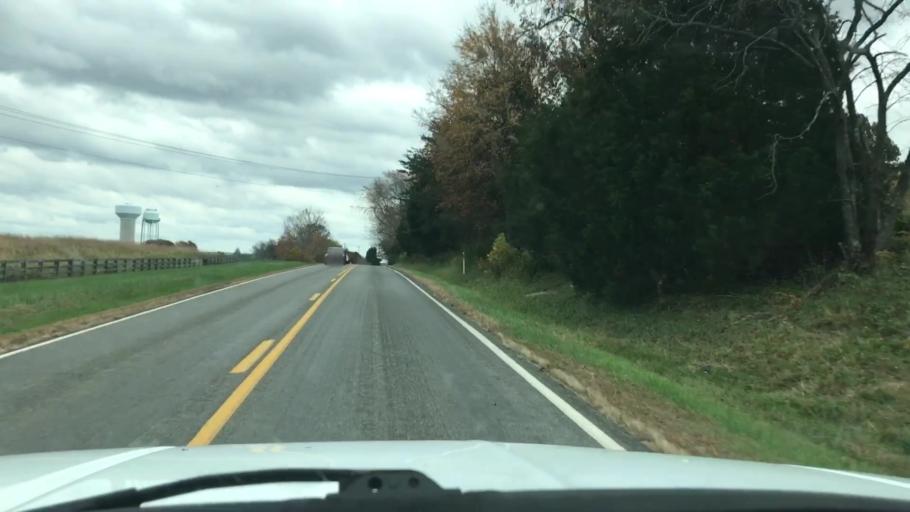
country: US
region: Virginia
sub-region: Goochland County
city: Goochland
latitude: 37.6507
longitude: -77.8432
